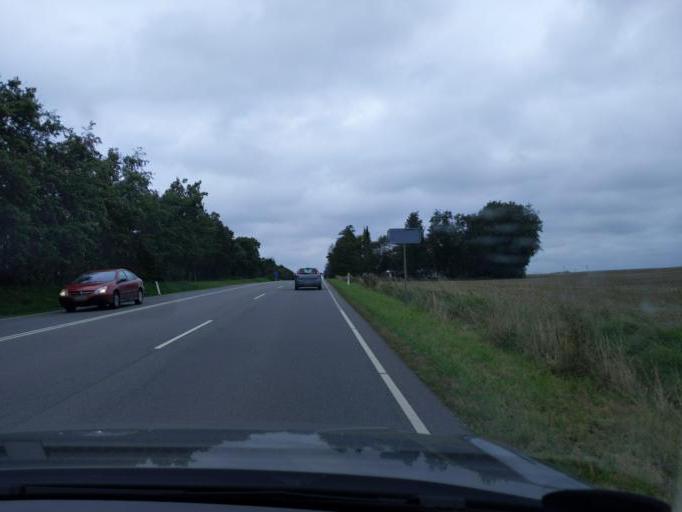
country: DK
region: North Denmark
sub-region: Mariagerfjord Kommune
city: Hobro
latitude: 56.5719
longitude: 9.8176
